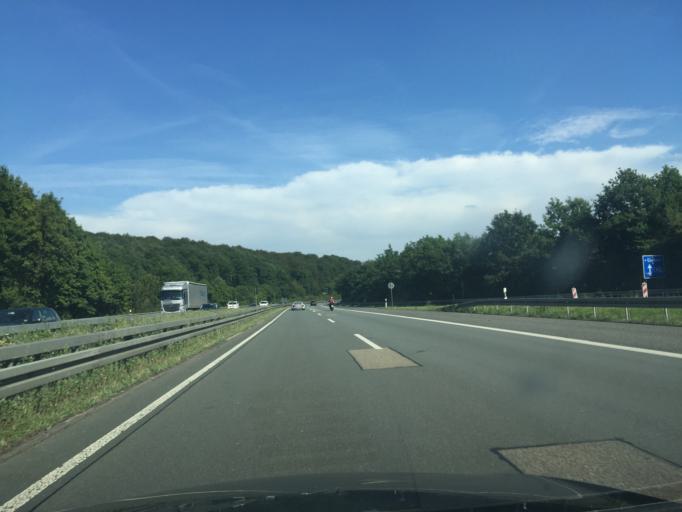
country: DE
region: Hesse
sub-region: Regierungsbezirk Giessen
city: Ehringshausen
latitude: 50.6212
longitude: 8.3654
